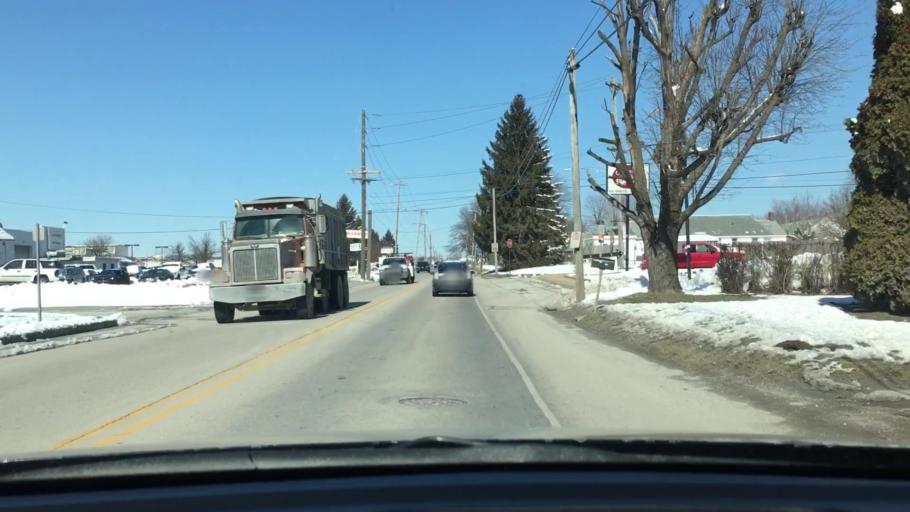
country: US
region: Pennsylvania
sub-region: York County
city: West York
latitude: 39.9720
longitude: -76.7523
